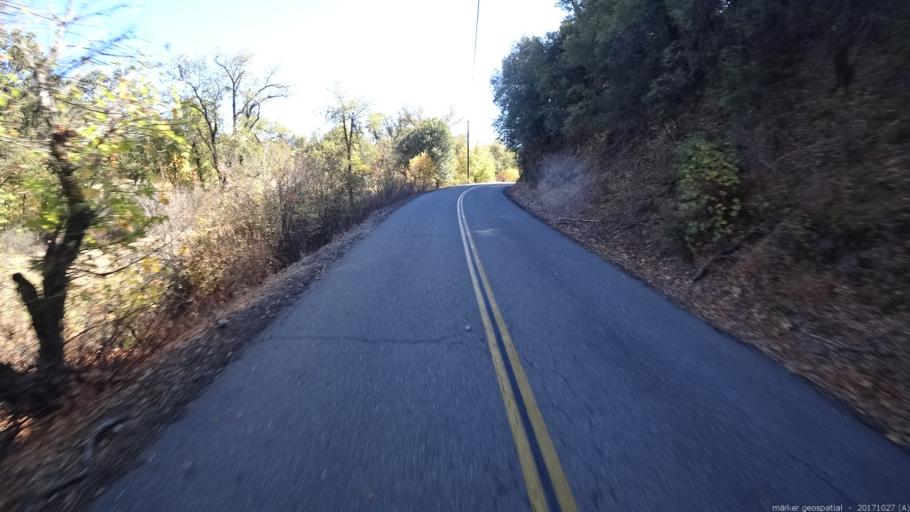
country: US
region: California
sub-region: Shasta County
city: Bella Vista
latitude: 40.7418
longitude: -122.0143
